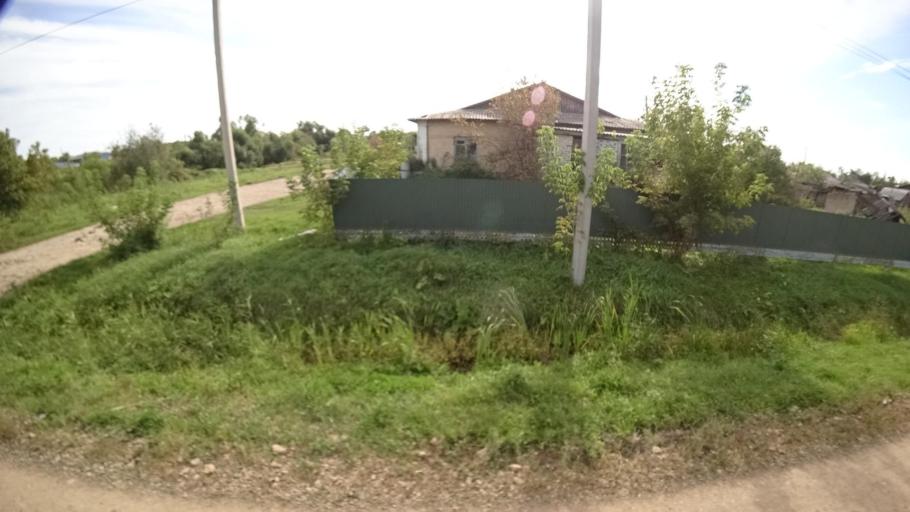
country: RU
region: Primorskiy
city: Dostoyevka
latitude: 44.3071
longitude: 133.4564
